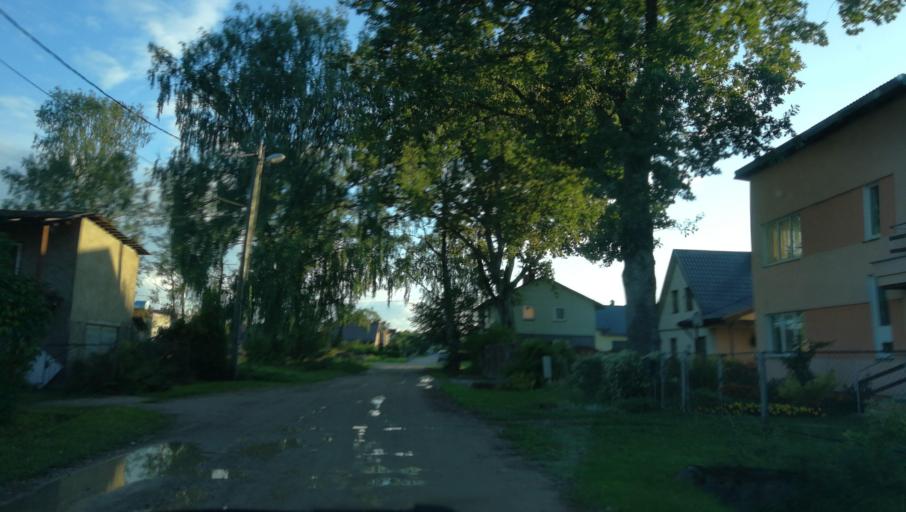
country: LV
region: Valmieras Rajons
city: Valmiera
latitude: 57.5346
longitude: 25.3947
